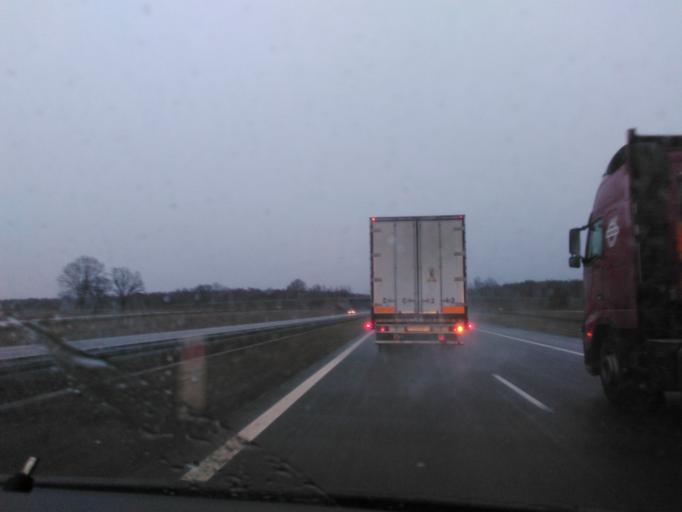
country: PL
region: Masovian Voivodeship
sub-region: Powiat minski
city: Ceglow
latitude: 52.2032
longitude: 21.7343
